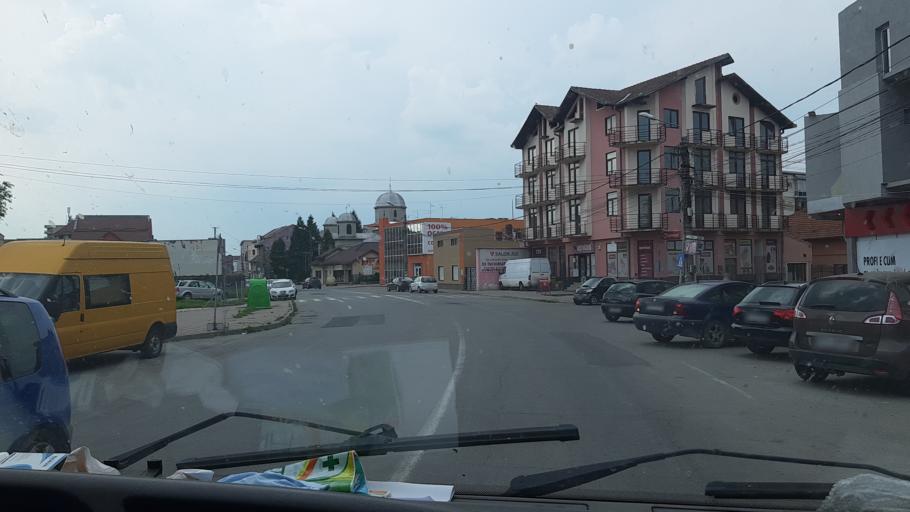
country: RO
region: Timis
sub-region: Municipiul Lugoj
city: Lugoj
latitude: 45.6945
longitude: 21.9019
